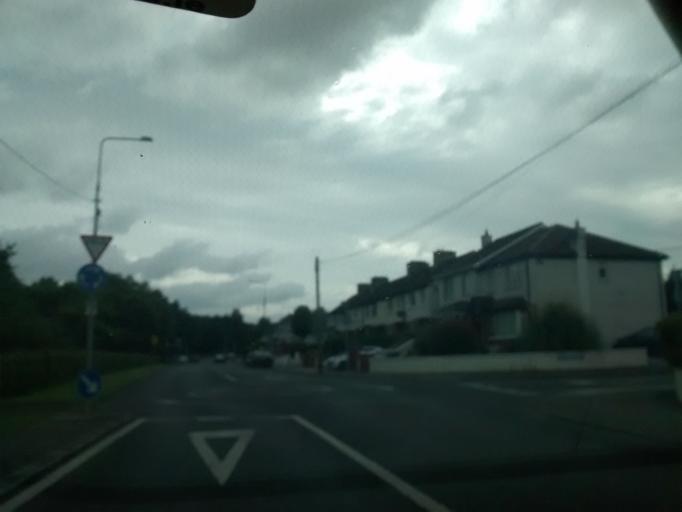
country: IE
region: Leinster
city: Dollymount
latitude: 53.3751
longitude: -6.1845
